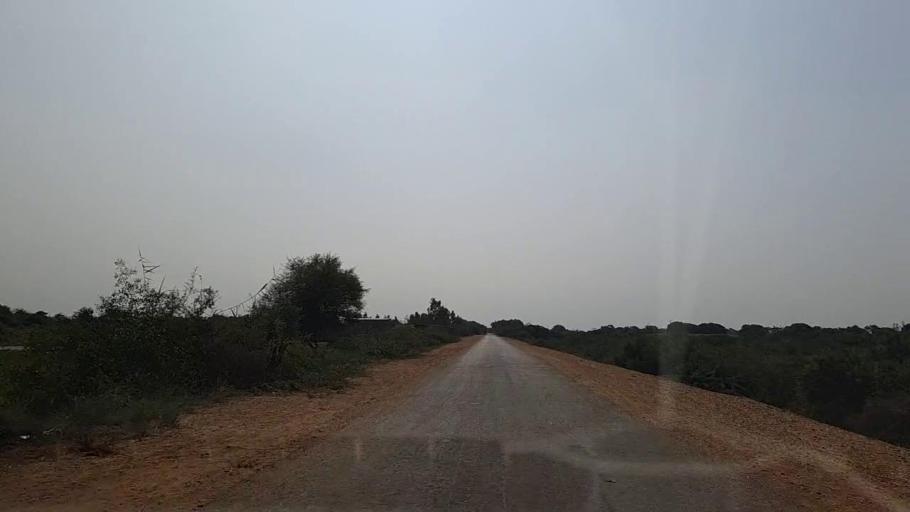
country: PK
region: Sindh
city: Chuhar Jamali
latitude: 24.2533
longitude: 67.9063
